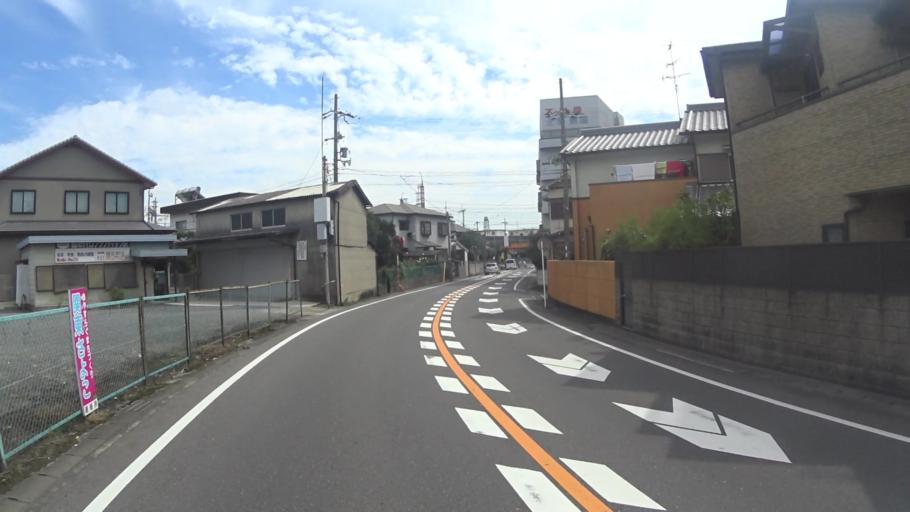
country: JP
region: Kyoto
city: Yawata
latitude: 34.8864
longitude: 135.7028
